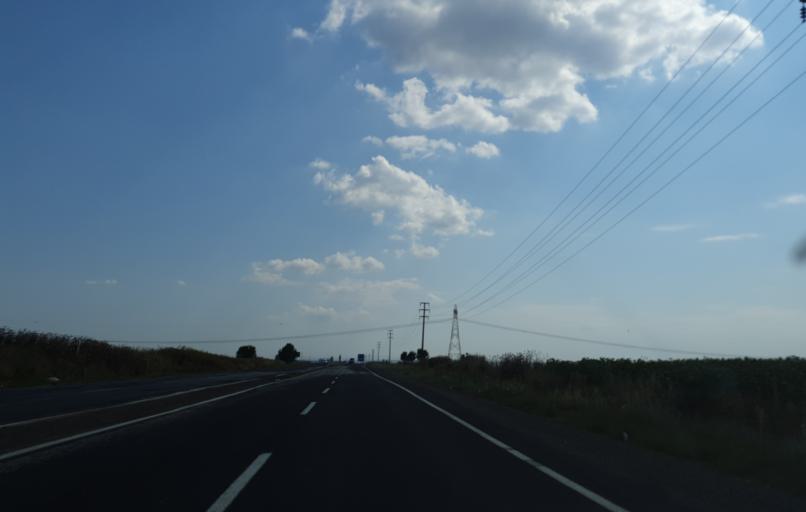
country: TR
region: Kirklareli
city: Buyukkaristiran
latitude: 41.2371
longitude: 27.5357
